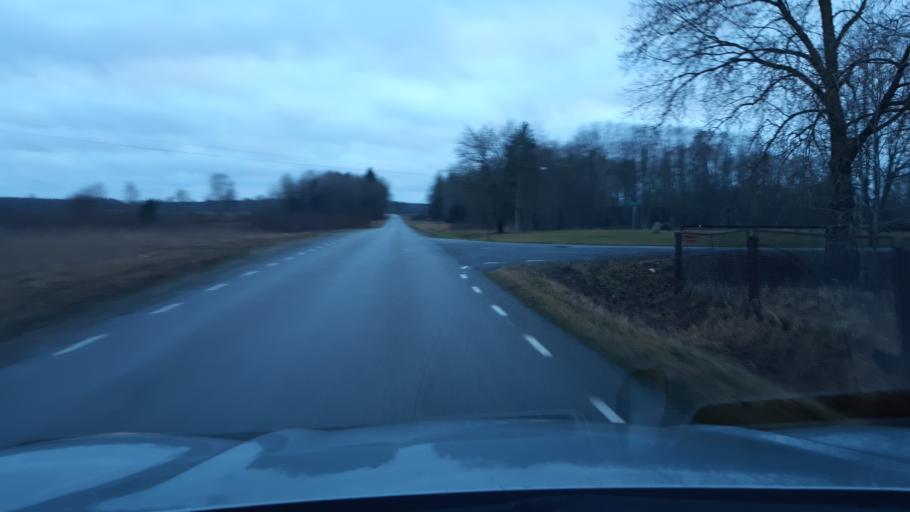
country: EE
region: Raplamaa
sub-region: Rapla vald
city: Rapla
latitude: 59.0413
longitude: 24.6770
